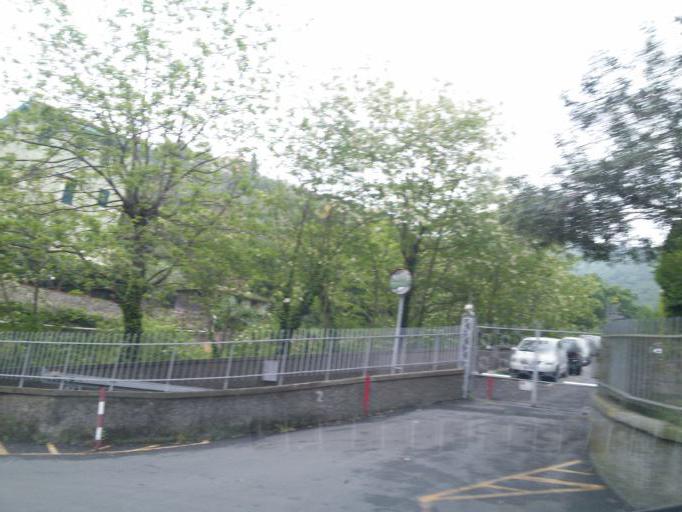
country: IT
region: Liguria
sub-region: Provincia di Genova
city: Genoa
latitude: 44.4203
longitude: 8.9745
